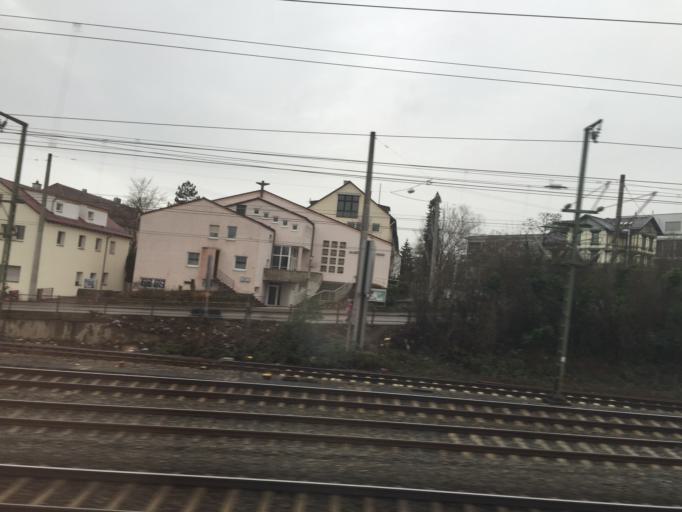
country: DE
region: Baden-Wuerttemberg
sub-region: Regierungsbezirk Stuttgart
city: Stuttgart Feuerbach
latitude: 48.8338
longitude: 9.1657
